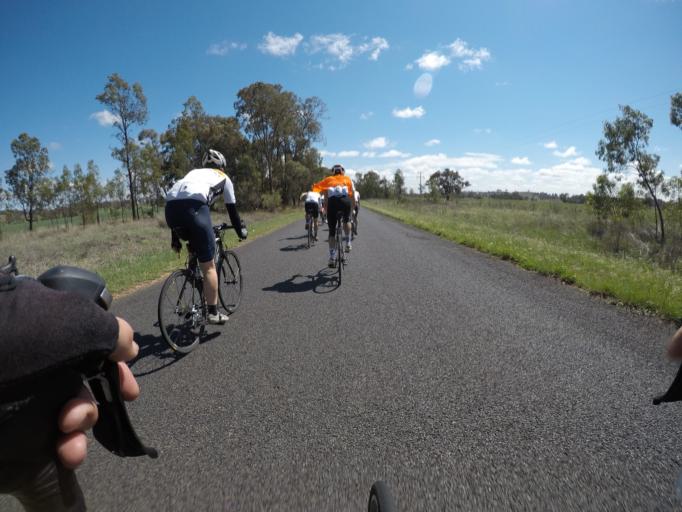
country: AU
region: New South Wales
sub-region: Dubbo Municipality
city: Dubbo
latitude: -32.5738
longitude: 148.5352
